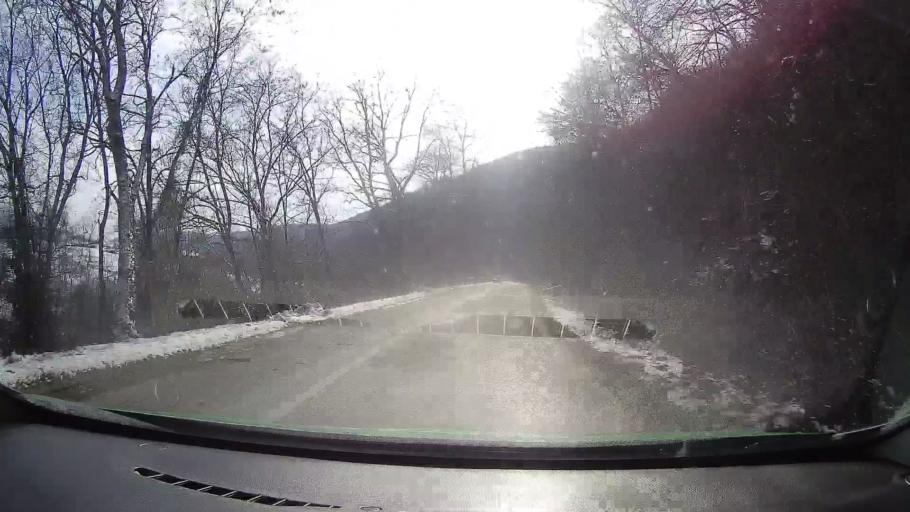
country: RO
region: Mures
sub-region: Comuna Apold
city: Saes
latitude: 46.1813
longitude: 24.7591
